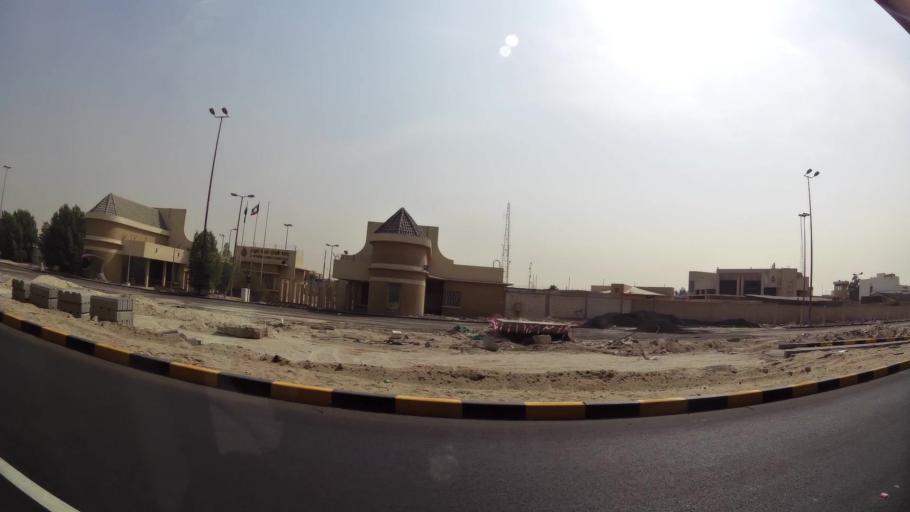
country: KW
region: Al Asimah
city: Ar Rabiyah
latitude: 29.3256
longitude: 47.9176
